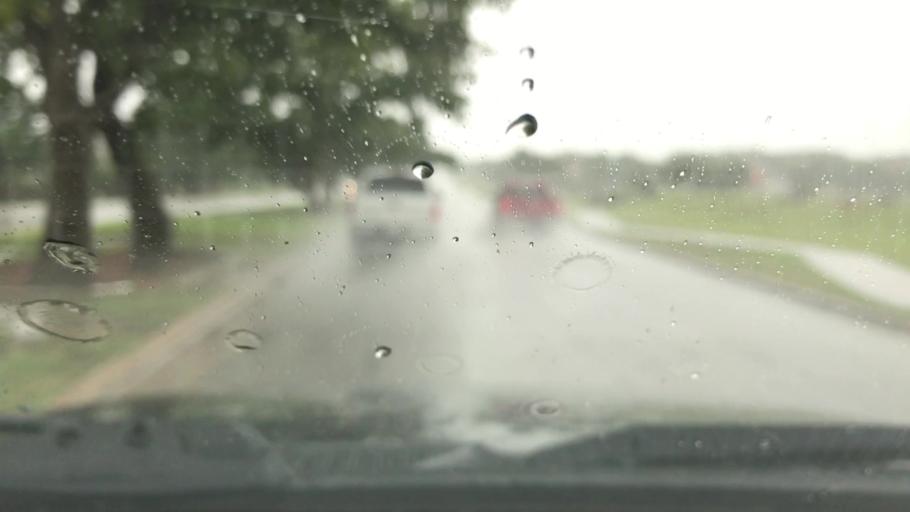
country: US
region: Texas
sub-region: Williamson County
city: Leander
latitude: 30.5370
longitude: -97.8612
